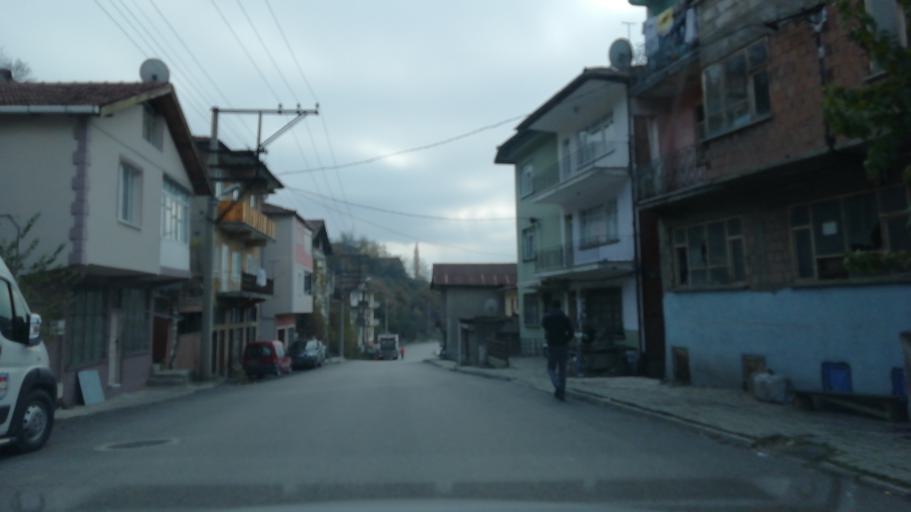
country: TR
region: Karabuk
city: Karabuk
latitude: 41.2127
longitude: 32.6287
